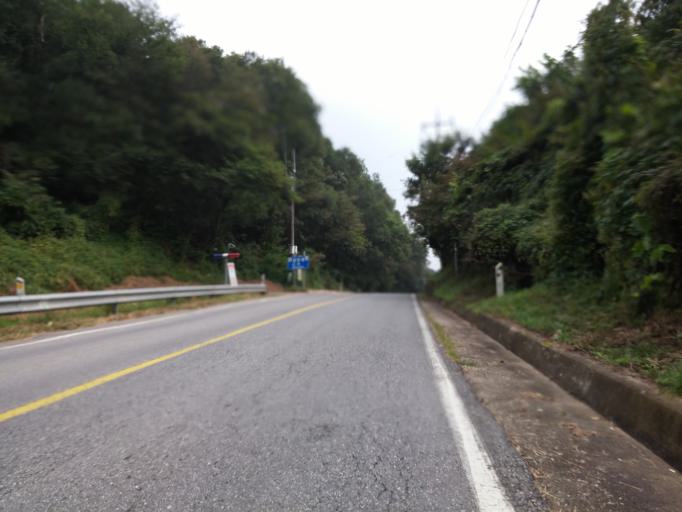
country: KR
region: Chungcheongbuk-do
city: Okcheon
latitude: 36.3974
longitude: 127.6874
